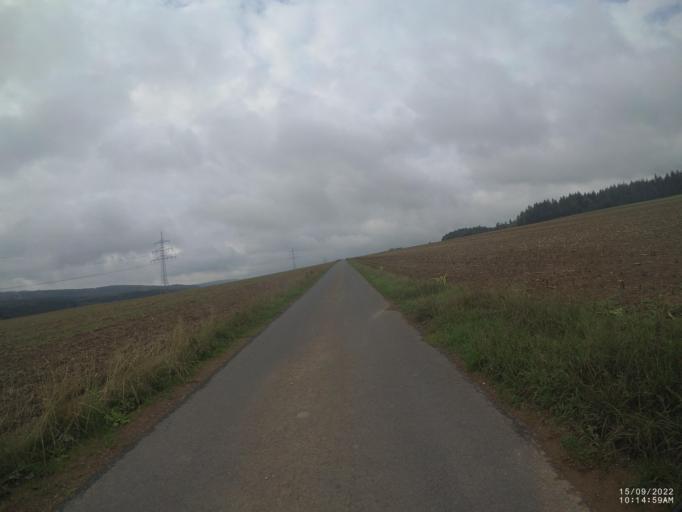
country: DE
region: Rheinland-Pfalz
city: Trierscheid
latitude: 50.3542
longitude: 6.8017
